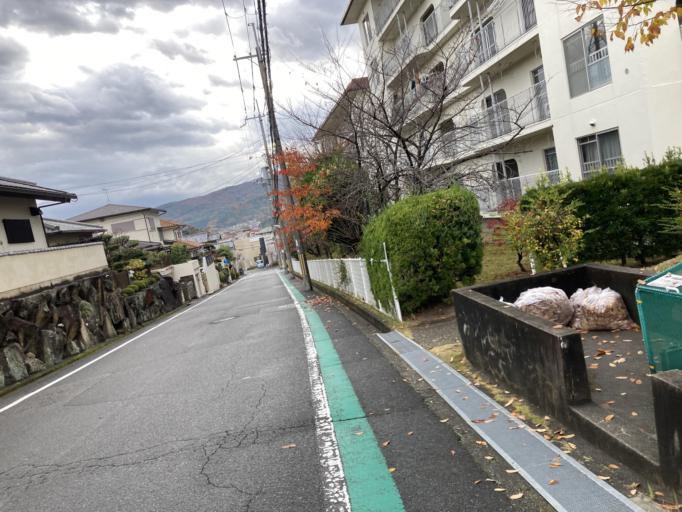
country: JP
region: Nara
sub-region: Ikoma-shi
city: Ikoma
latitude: 34.6833
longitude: 135.7130
